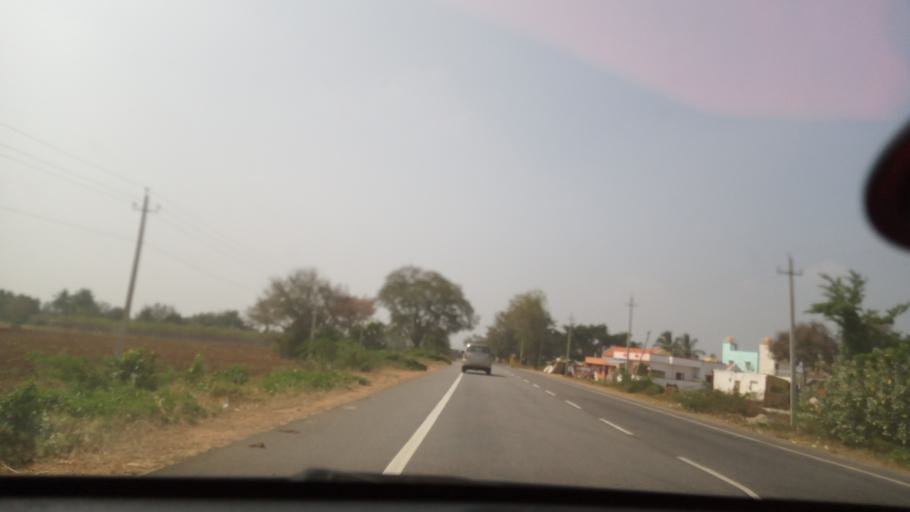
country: IN
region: Karnataka
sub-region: Mysore
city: Nanjangud
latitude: 12.0666
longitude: 76.7513
